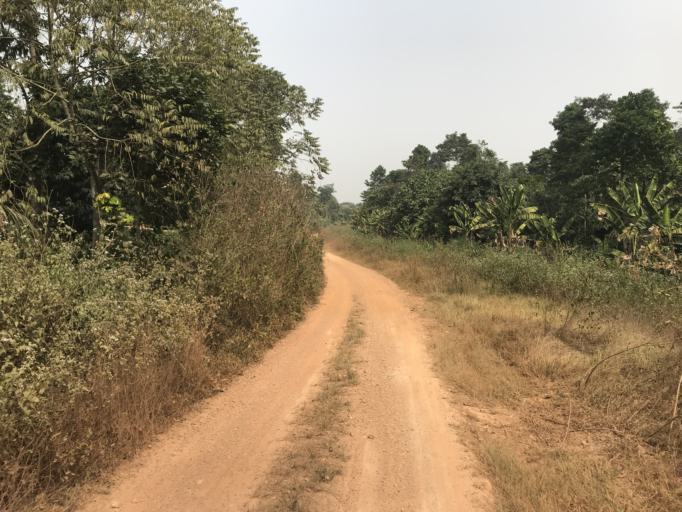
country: NG
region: Osun
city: Ifetedo
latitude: 7.0429
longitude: 4.4615
